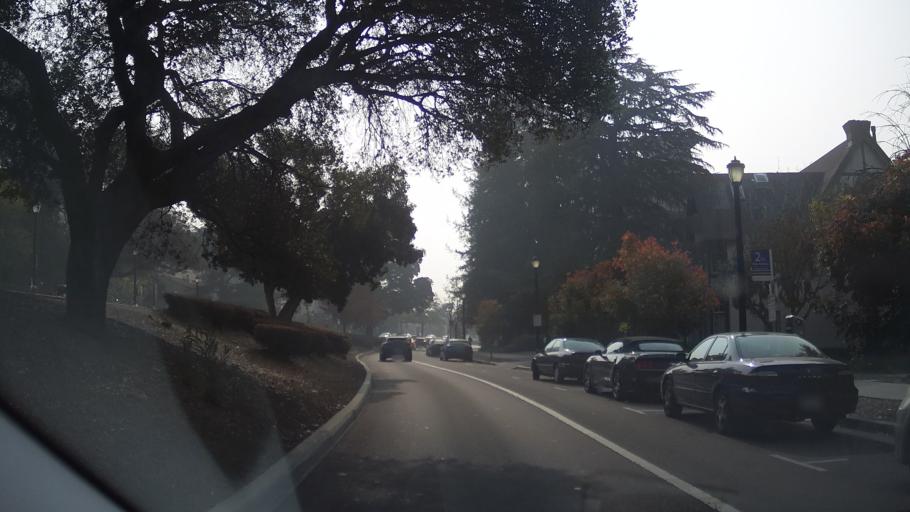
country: US
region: California
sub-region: Alameda County
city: Berkeley
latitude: 37.8709
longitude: -122.2527
